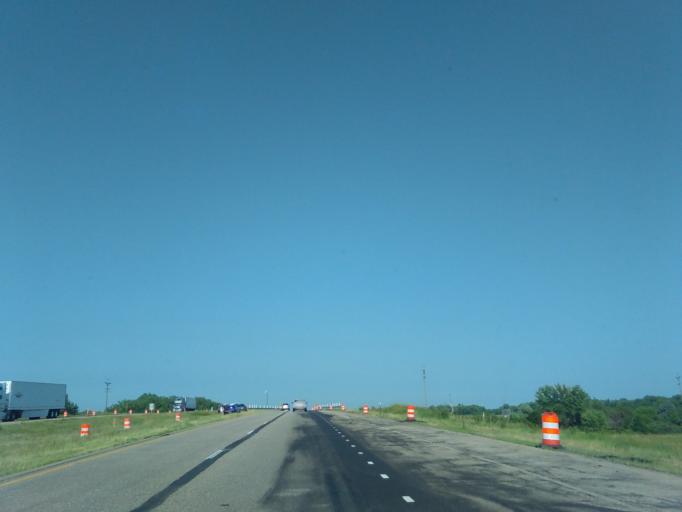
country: US
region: Nebraska
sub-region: Hall County
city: Grand Island
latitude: 40.8214
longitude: -98.3713
